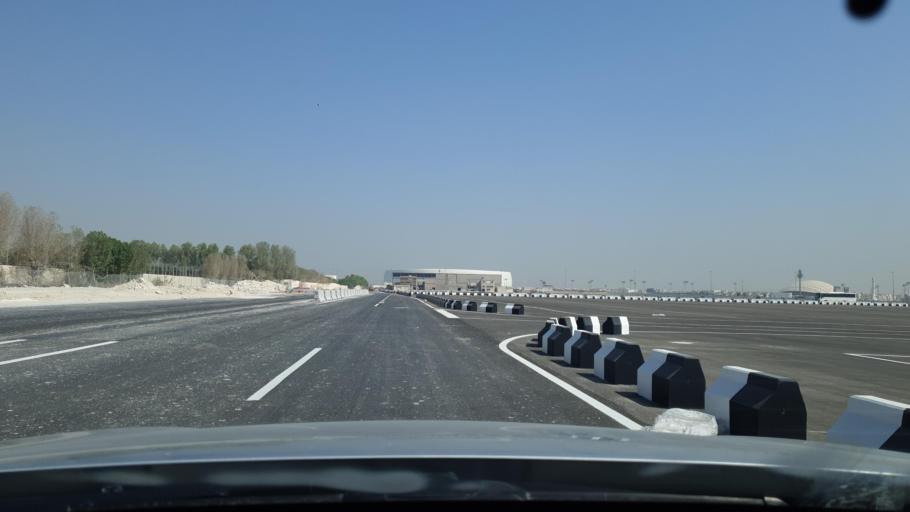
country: QA
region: Baladiyat ad Dawhah
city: Doha
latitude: 25.2244
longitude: 51.5263
